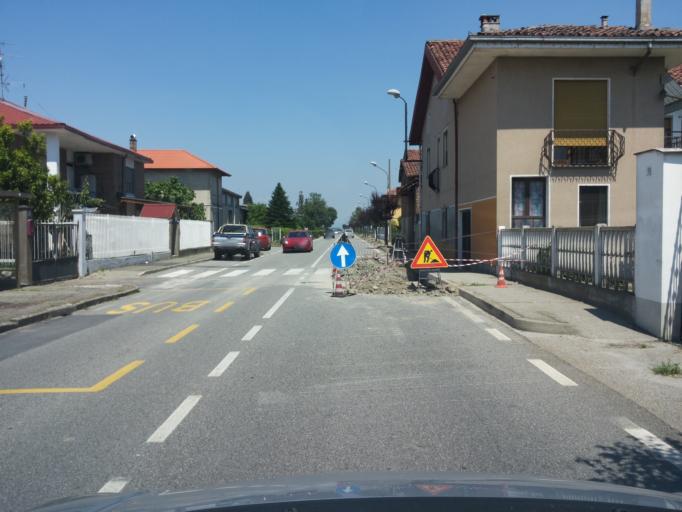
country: IT
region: Piedmont
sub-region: Provincia di Novara
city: Casalvolone
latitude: 45.4023
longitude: 8.4638
